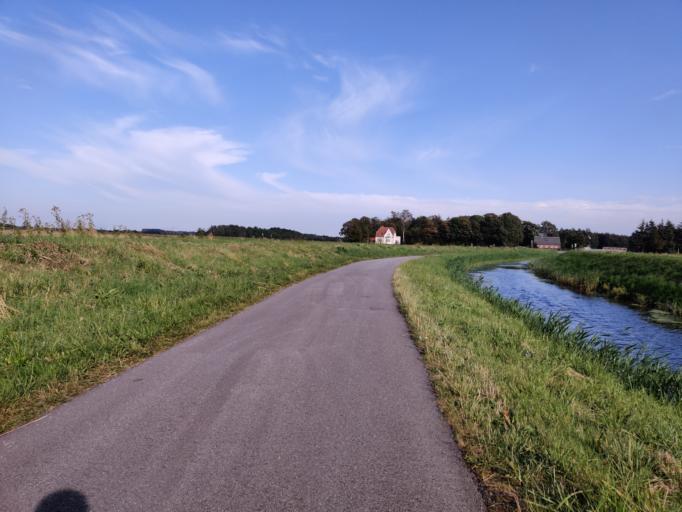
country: DK
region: Zealand
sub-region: Guldborgsund Kommune
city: Nykobing Falster
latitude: 54.6842
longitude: 11.9027
